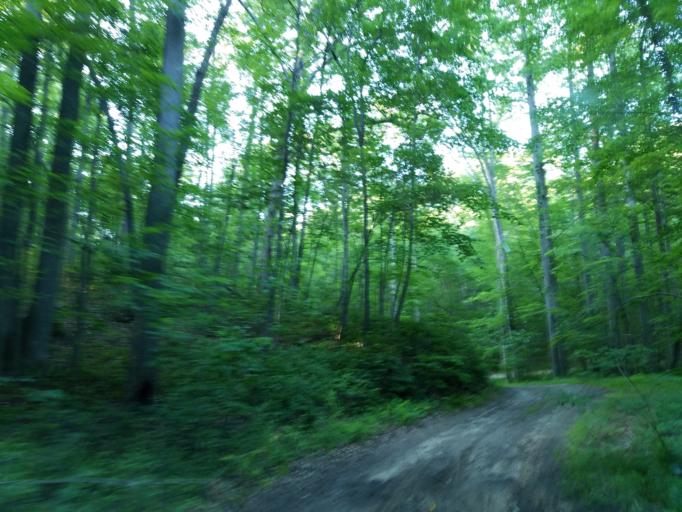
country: US
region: Georgia
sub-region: Fannin County
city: Blue Ridge
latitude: 34.8163
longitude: -84.1510
